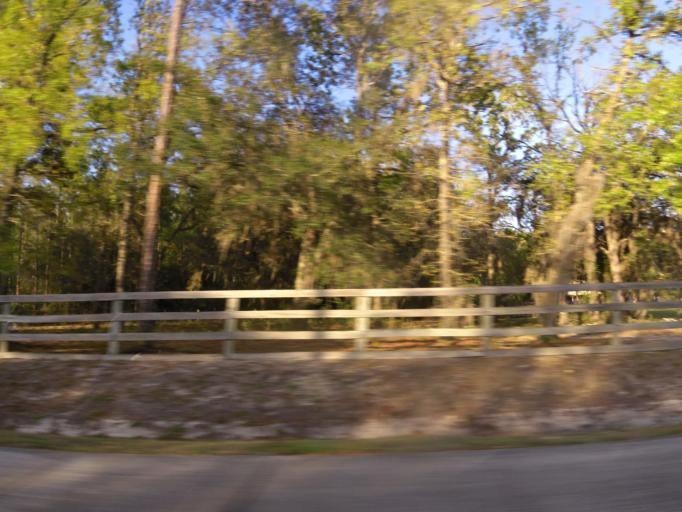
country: US
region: Florida
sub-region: Saint Johns County
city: Fruit Cove
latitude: 30.0743
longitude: -81.5174
